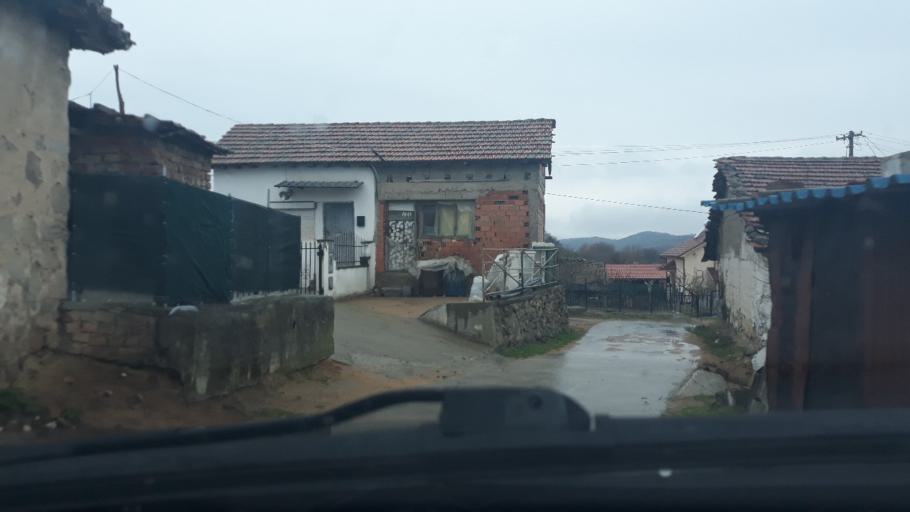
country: MK
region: Bogdanci
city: Bogdanci
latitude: 41.2388
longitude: 22.6123
